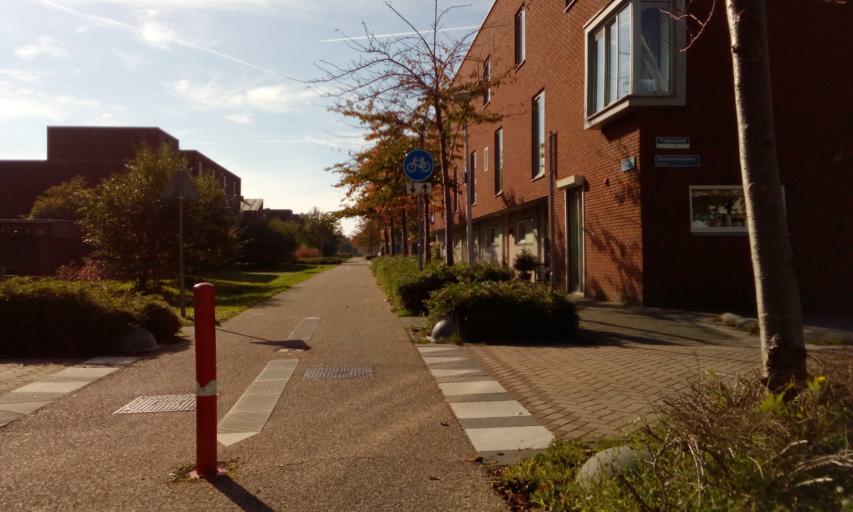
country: NL
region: Utrecht
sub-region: Stichtse Vecht
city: Spechtenkamp
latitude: 52.0825
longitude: 5.0233
